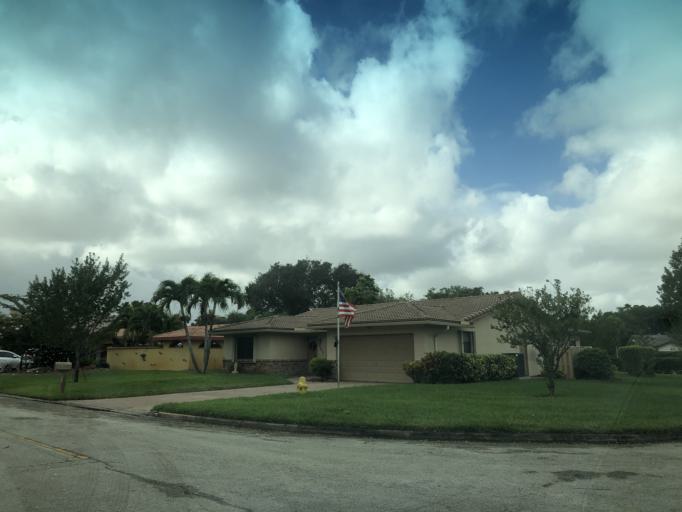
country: US
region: Florida
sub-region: Broward County
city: Margate
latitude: 26.2515
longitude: -80.2395
